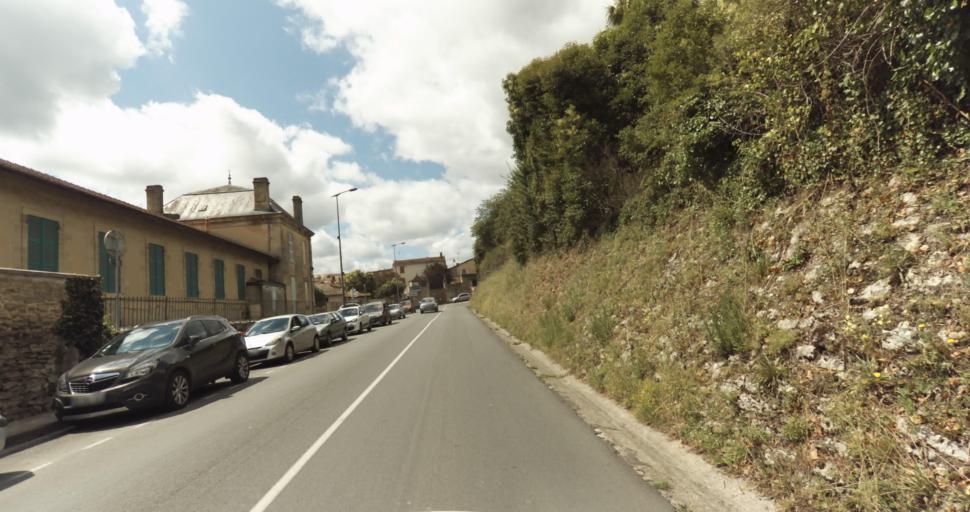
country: FR
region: Aquitaine
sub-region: Departement de la Gironde
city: Bazas
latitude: 44.4335
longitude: -0.2116
